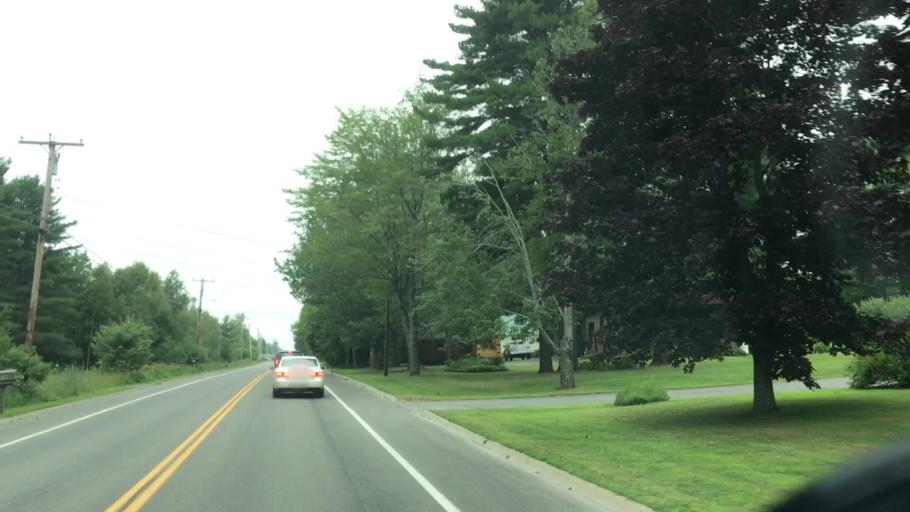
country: US
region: Maine
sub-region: Penobscot County
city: Veazie
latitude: 44.8478
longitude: -68.7385
